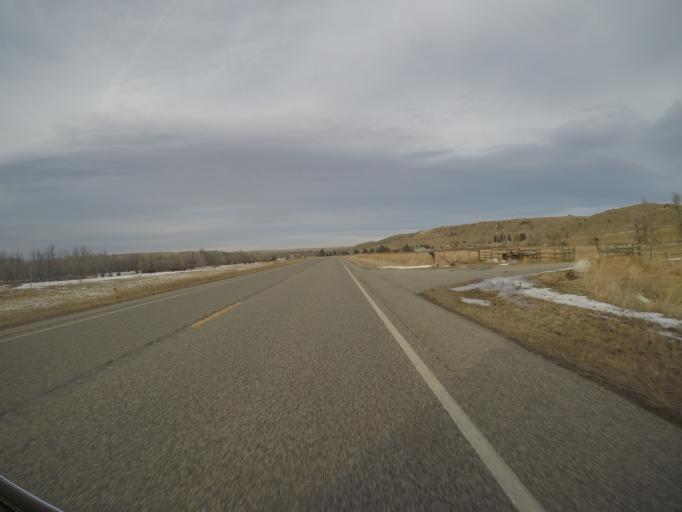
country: US
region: Montana
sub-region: Stillwater County
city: Absarokee
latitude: 45.4751
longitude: -109.4488
